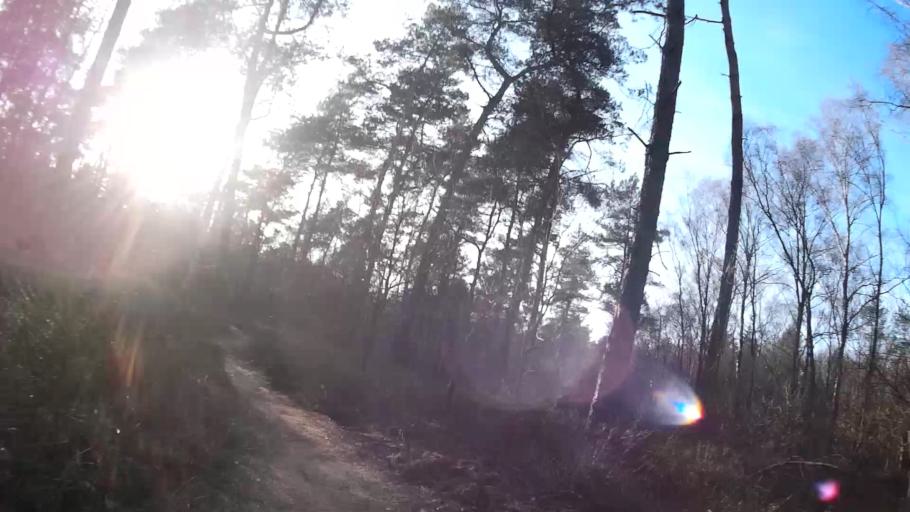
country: NL
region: Utrecht
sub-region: Gemeente Rhenen
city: Rhenen
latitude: 51.9790
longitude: 5.5578
